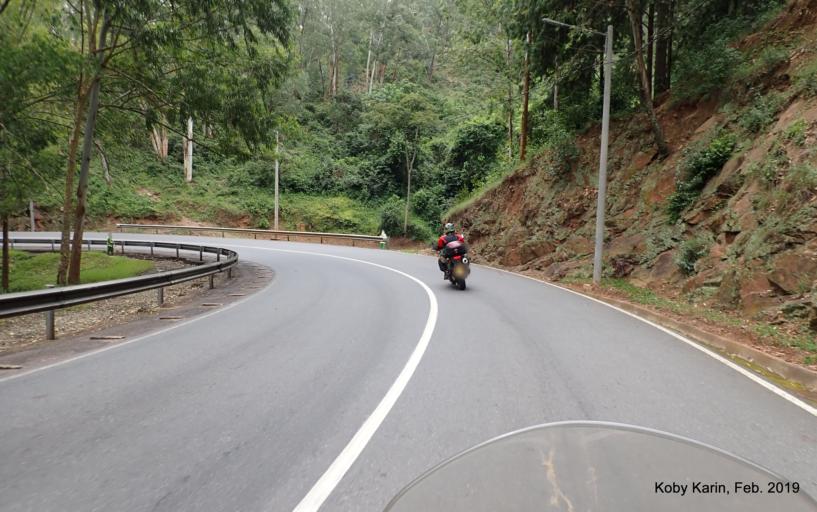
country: RW
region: Kigali
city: Kigali
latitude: -1.9316
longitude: 30.0254
